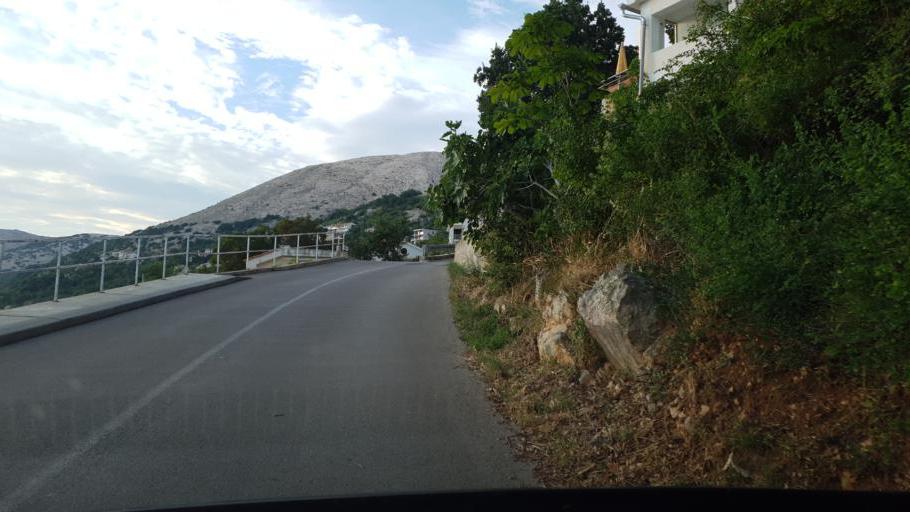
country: HR
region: Primorsko-Goranska
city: Punat
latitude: 44.9541
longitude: 14.6897
